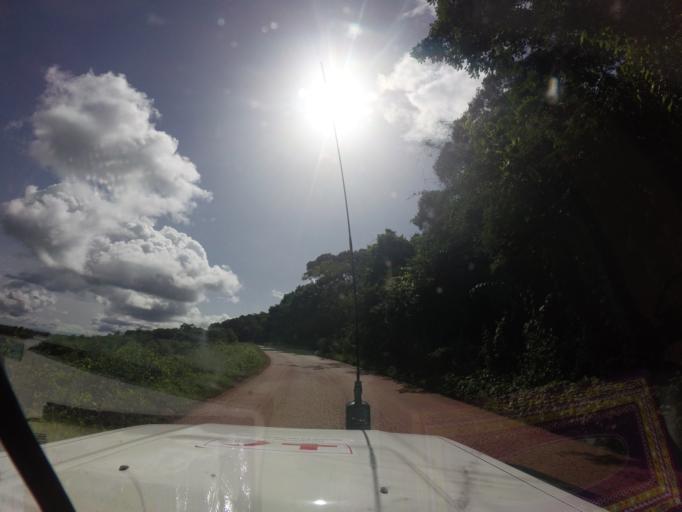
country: GN
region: Mamou
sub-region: Mamou Prefecture
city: Mamou
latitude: 10.3652
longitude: -12.1302
